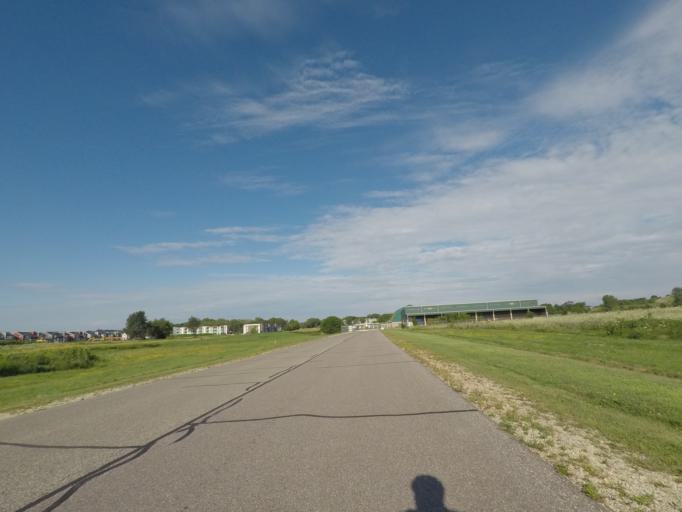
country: US
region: Wisconsin
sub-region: Dane County
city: Middleton
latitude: 43.0540
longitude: -89.5537
